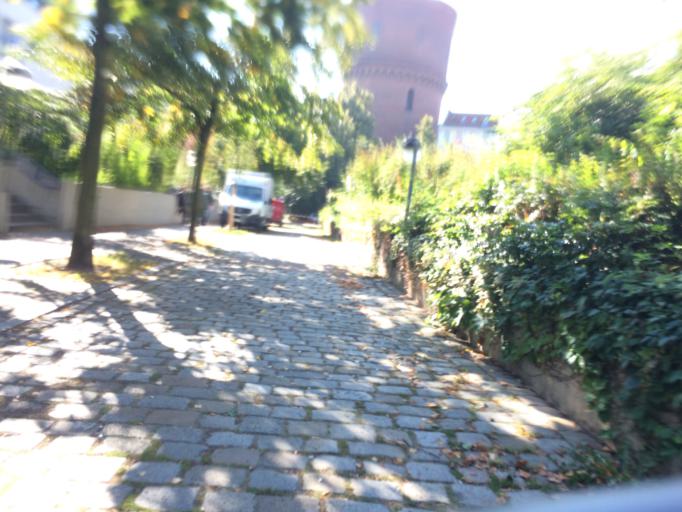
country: DE
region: Berlin
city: Berlin Treptow
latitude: 52.4765
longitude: 13.4293
